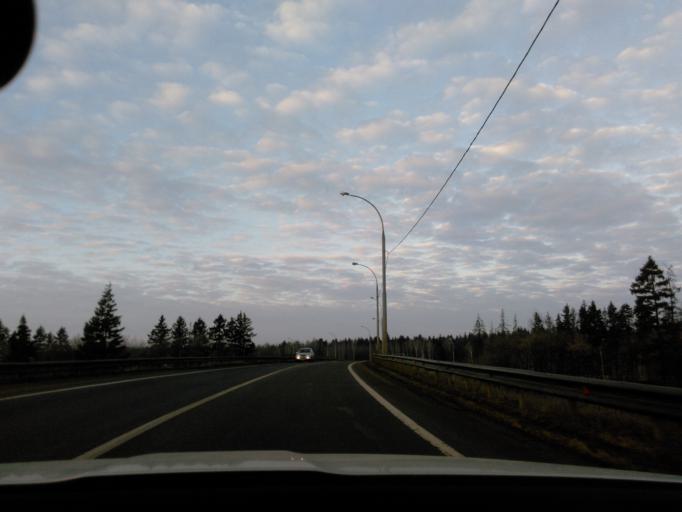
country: RU
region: Moskovskaya
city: Novopodrezkovo
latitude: 55.9676
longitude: 37.3273
